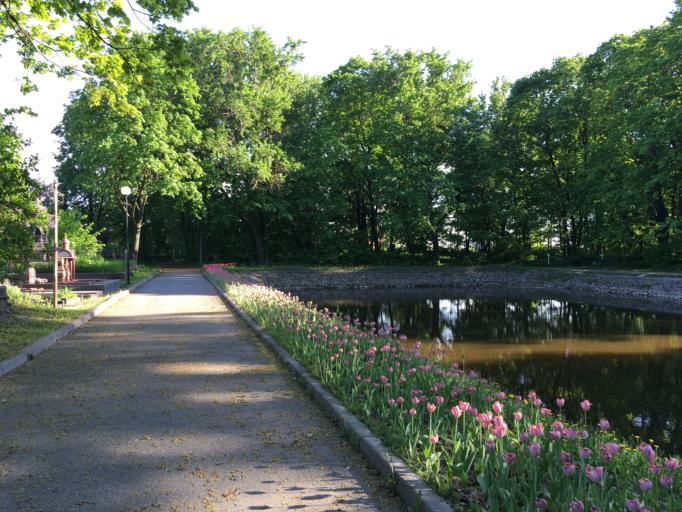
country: RU
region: St.-Petersburg
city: Admiralteisky
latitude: 59.8886
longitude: 30.3047
